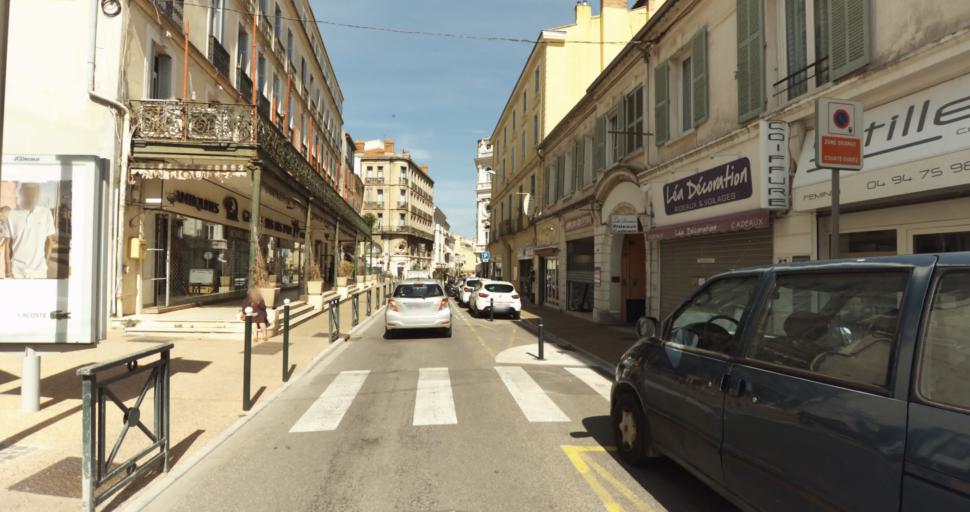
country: FR
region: Provence-Alpes-Cote d'Azur
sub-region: Departement du Var
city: Hyeres
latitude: 43.1201
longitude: 6.1265
